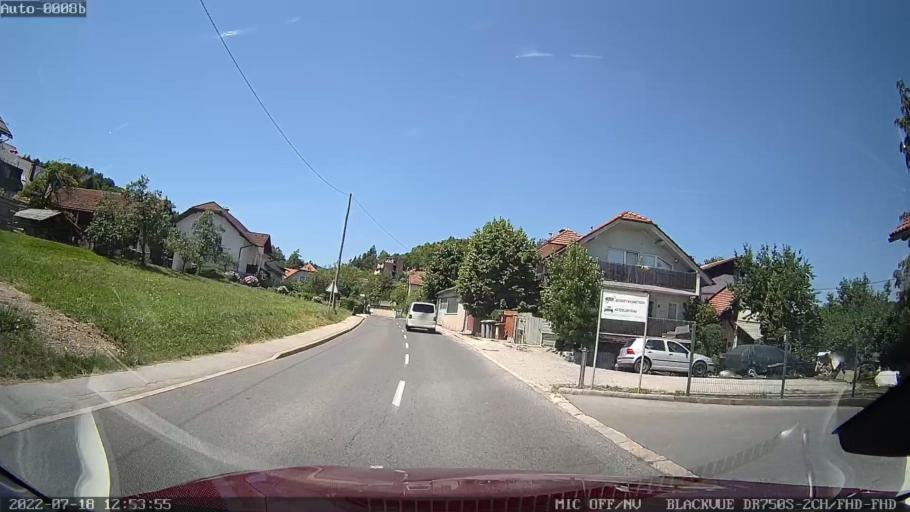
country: SI
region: Ljubljana
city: Ljubljana
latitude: 46.0745
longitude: 14.4477
